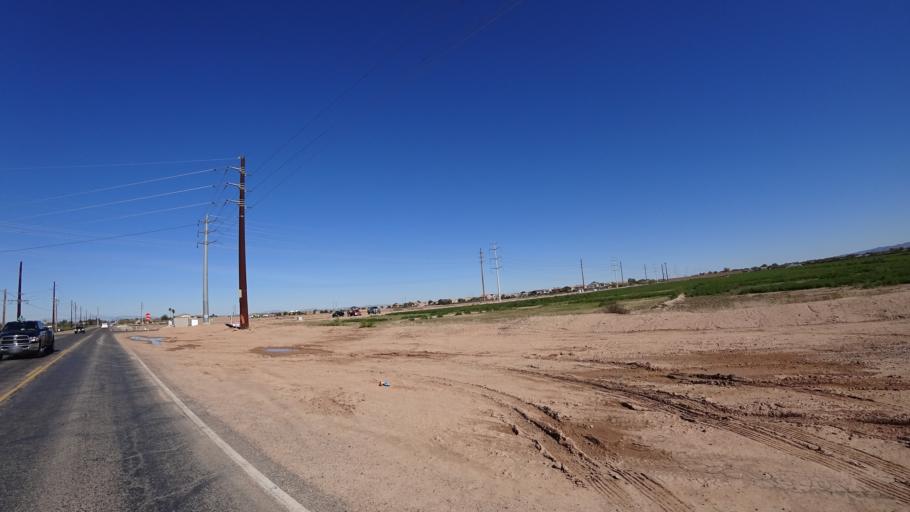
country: US
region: Arizona
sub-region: Maricopa County
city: Tolleson
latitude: 33.4055
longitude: -112.2893
